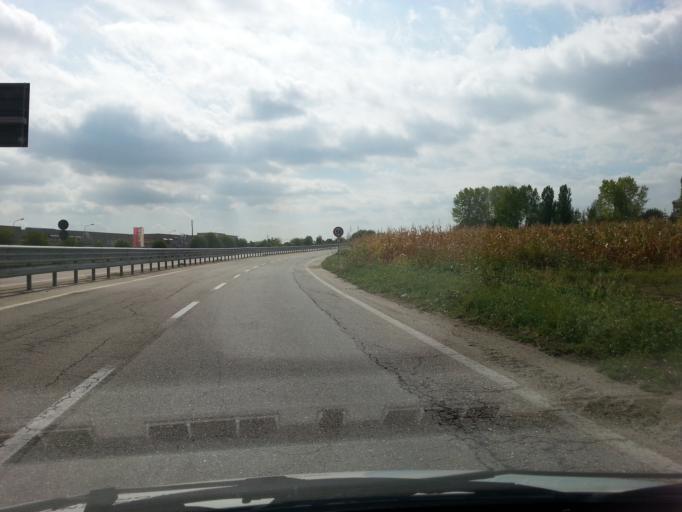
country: IT
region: Piedmont
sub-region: Provincia di Torino
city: Riva
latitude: 44.9005
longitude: 7.3602
